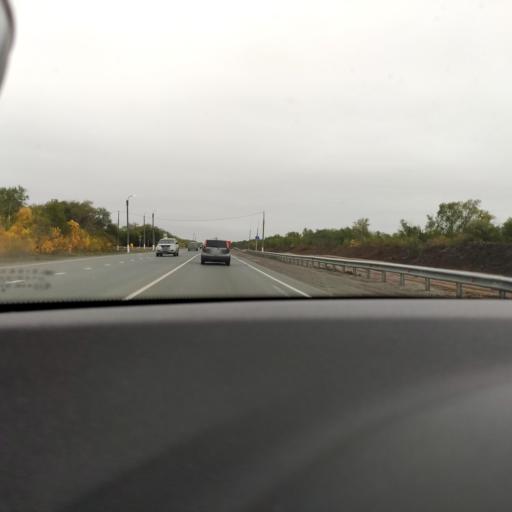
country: RU
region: Samara
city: Krasnyy Yar
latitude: 53.4564
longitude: 50.3889
